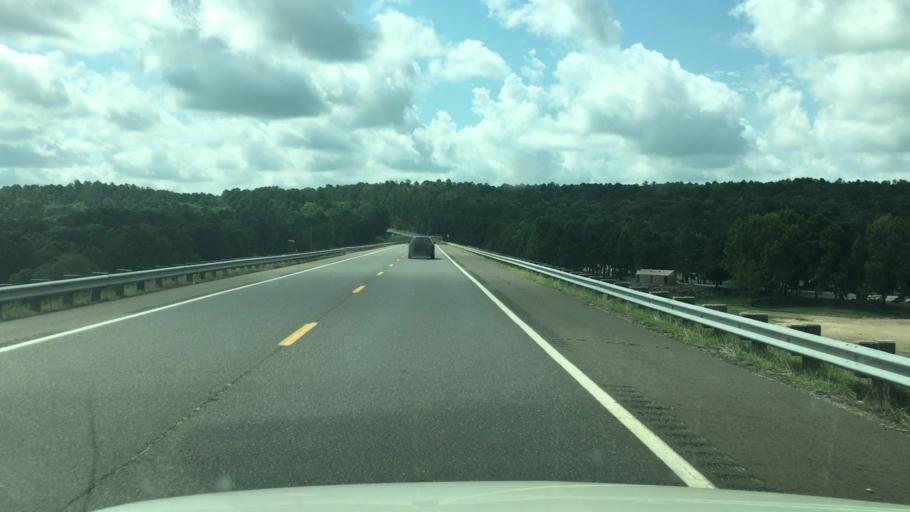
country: US
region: Arkansas
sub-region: Clark County
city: Arkadelphia
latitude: 34.2383
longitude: -93.1029
